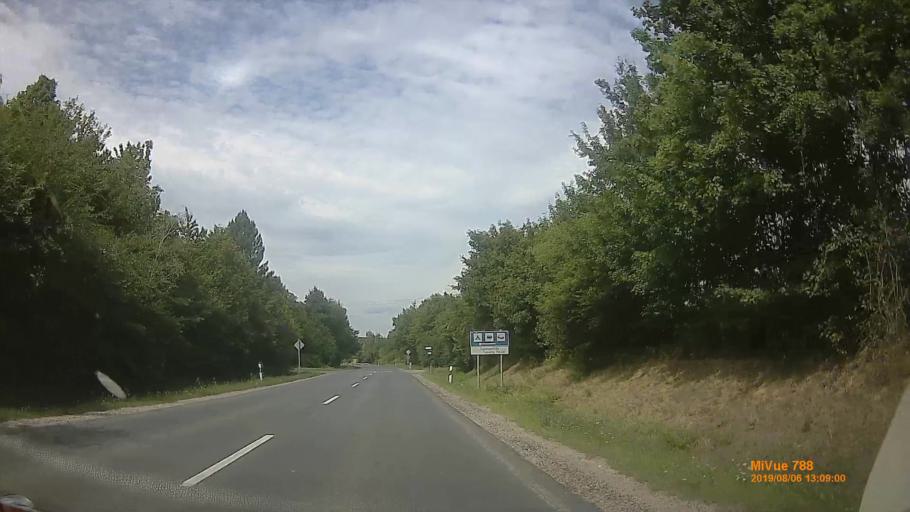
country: HU
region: Vas
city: Koszeg
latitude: 47.3947
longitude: 16.5507
